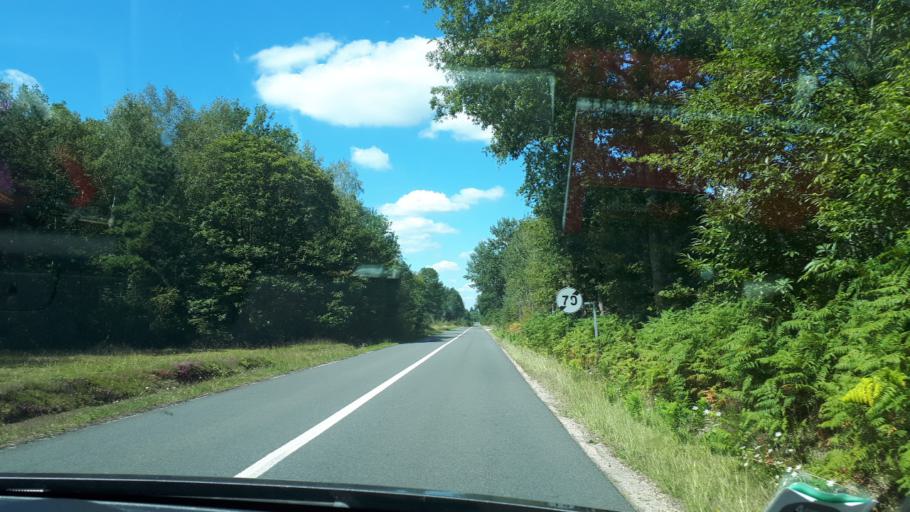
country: FR
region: Centre
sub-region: Departement du Loir-et-Cher
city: Neung-sur-Beuvron
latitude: 47.5342
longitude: 1.8345
